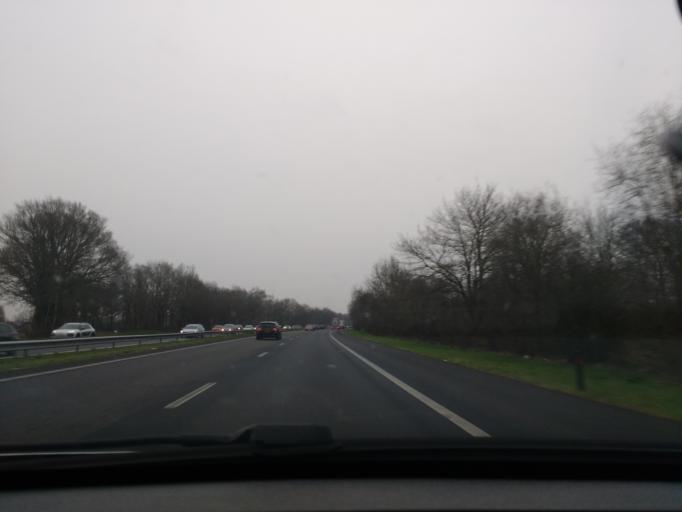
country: NL
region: Gelderland
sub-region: Gemeente Ede
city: Lunteren
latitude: 52.1012
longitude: 5.5876
